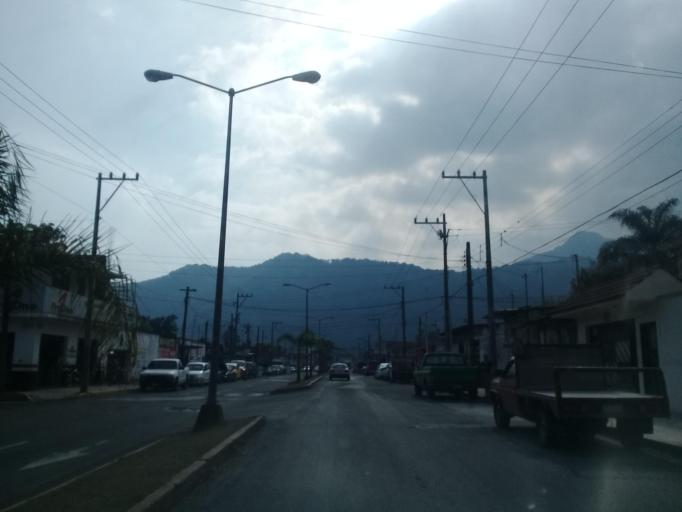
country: MX
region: Veracruz
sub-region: Ixhuatlancillo
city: Union y Progreso
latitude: 18.8706
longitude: -97.1115
